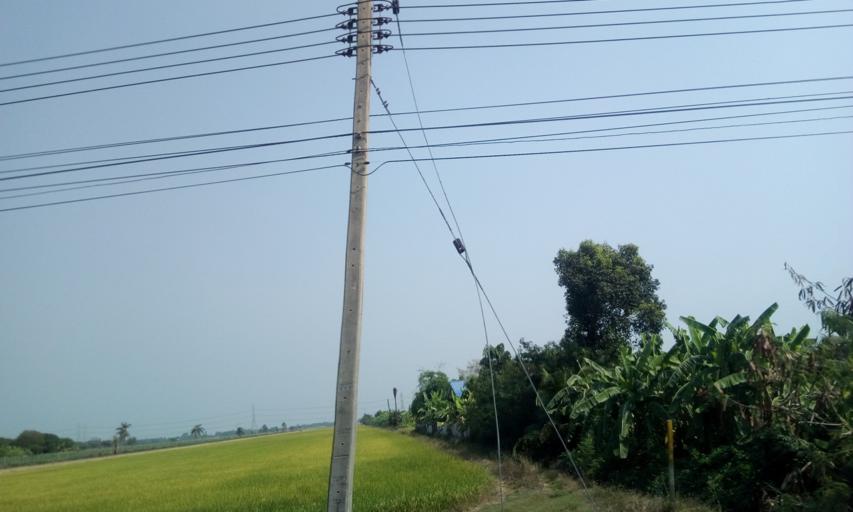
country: TH
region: Pathum Thani
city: Ban Rangsit
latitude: 14.0006
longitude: 100.7567
